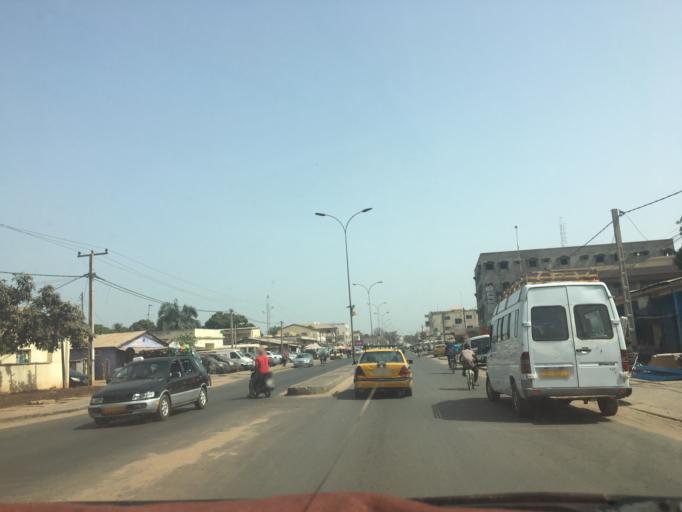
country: GM
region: Western
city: Abuko
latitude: 13.4343
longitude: -16.6759
